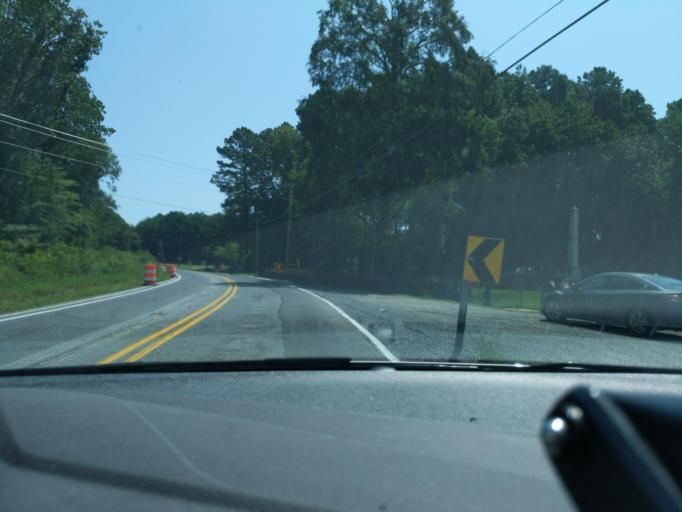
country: US
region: Virginia
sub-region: Northumberland County
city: Heathsville
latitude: 38.0738
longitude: -76.3426
